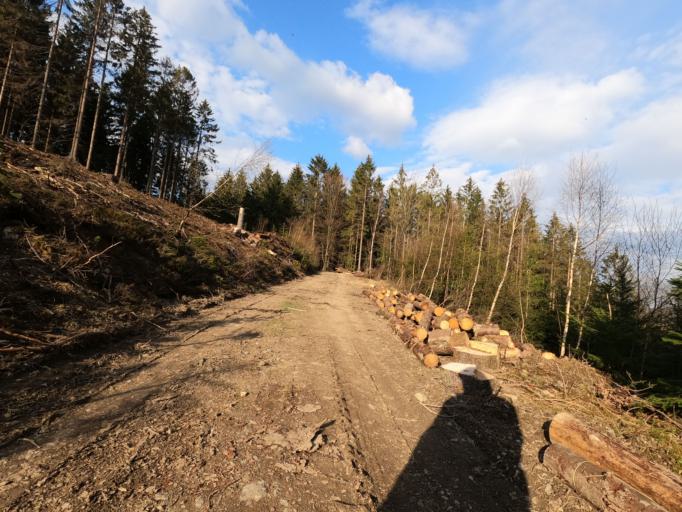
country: DE
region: North Rhine-Westphalia
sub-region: Regierungsbezirk Arnsberg
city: Herscheid
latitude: 51.1775
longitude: 7.7599
